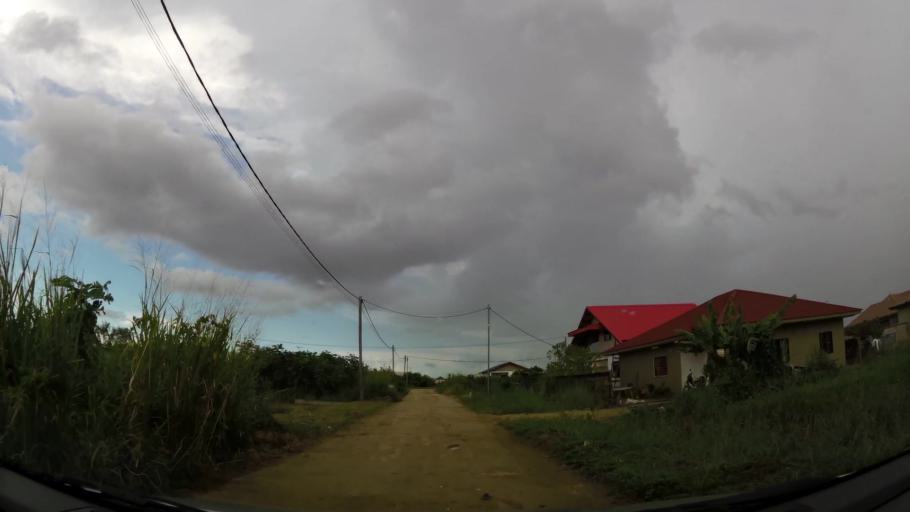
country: SR
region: Commewijne
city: Nieuw Amsterdam
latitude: 5.8516
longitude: -55.1162
